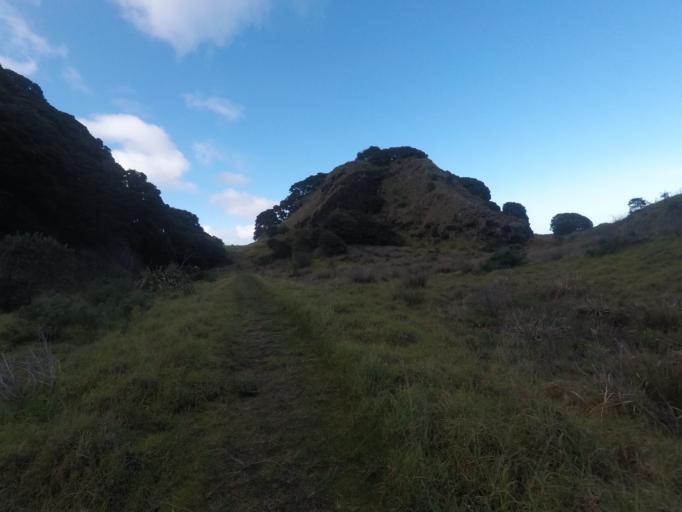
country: NZ
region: Auckland
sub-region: Auckland
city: Titirangi
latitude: -37.0022
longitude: 174.4804
